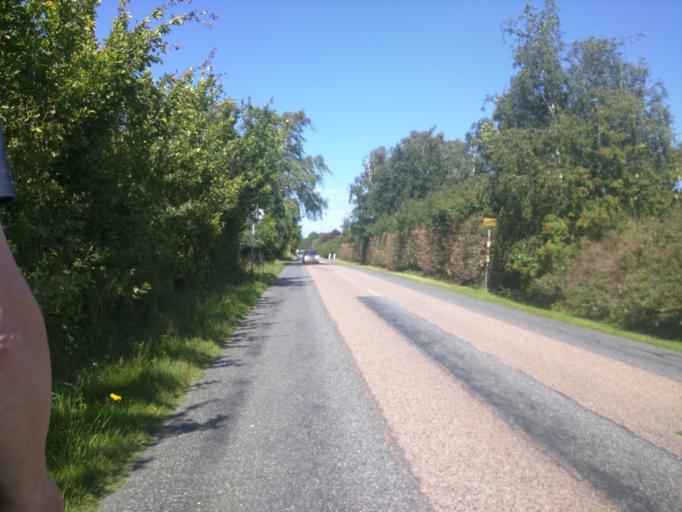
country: DK
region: Zealand
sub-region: Kalundborg Kommune
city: Svebolle
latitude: 55.6898
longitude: 11.2469
